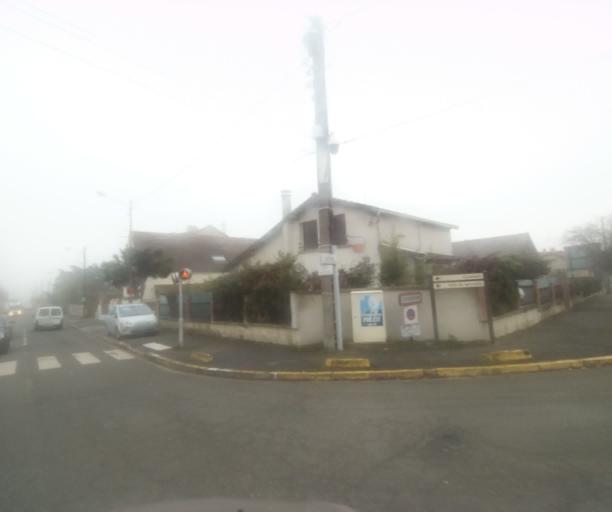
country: FR
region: Ile-de-France
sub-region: Departement de Seine-Saint-Denis
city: Coubron
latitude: 48.9107
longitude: 2.5839
